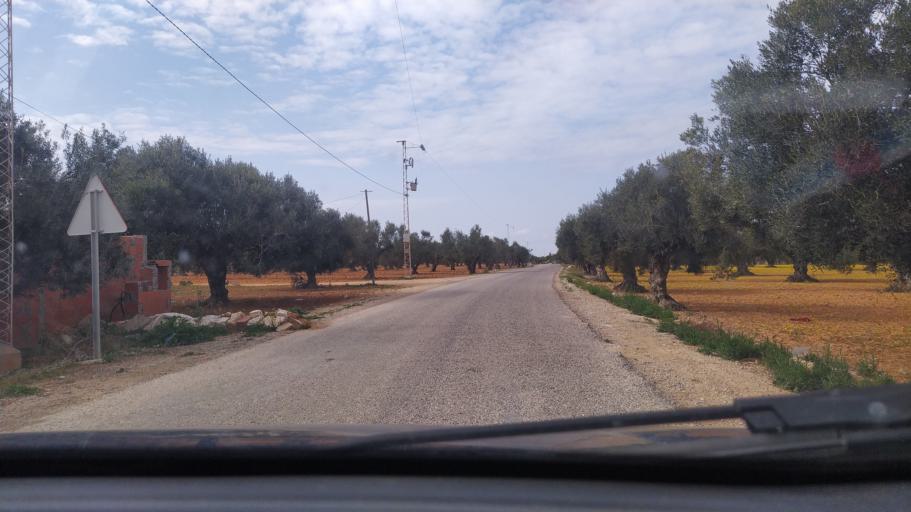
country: TN
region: Al Munastir
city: Sidi Bin Nur
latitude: 35.5273
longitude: 10.9646
